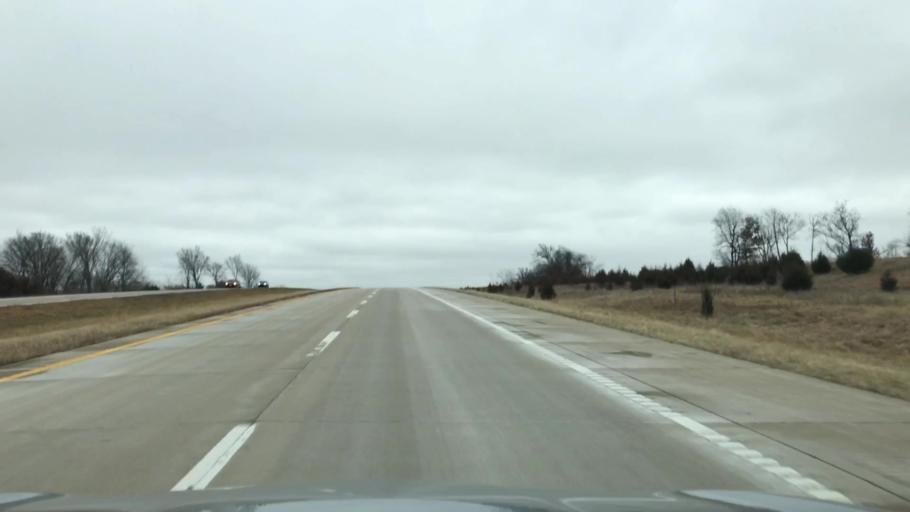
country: US
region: Missouri
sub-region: Livingston County
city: Chillicothe
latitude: 39.7357
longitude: -93.7479
